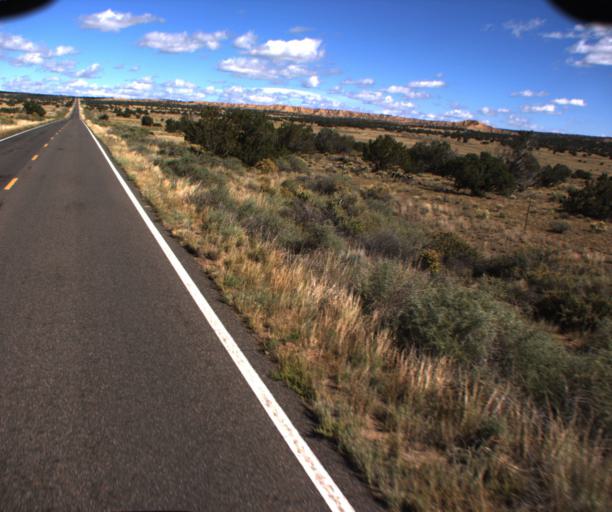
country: US
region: Arizona
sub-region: Apache County
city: Saint Johns
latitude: 34.7924
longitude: -109.2381
